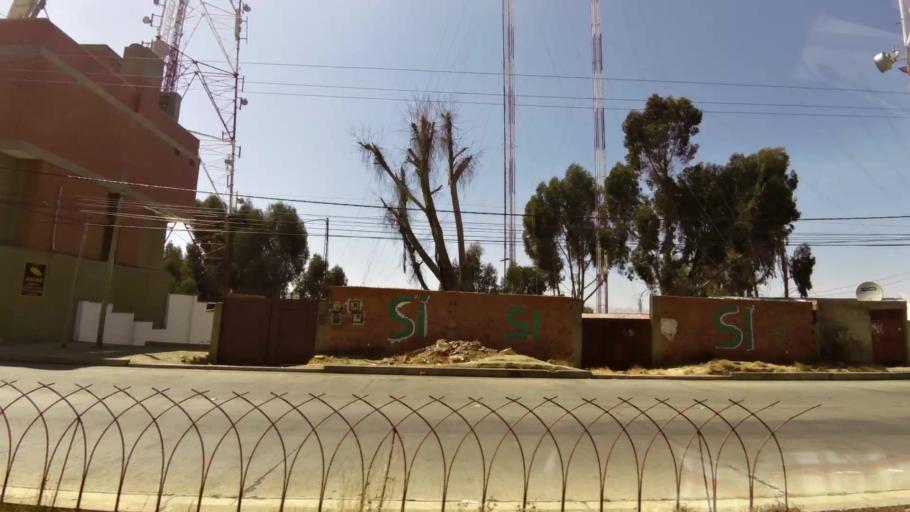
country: BO
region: La Paz
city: La Paz
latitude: -16.5272
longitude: -68.1459
